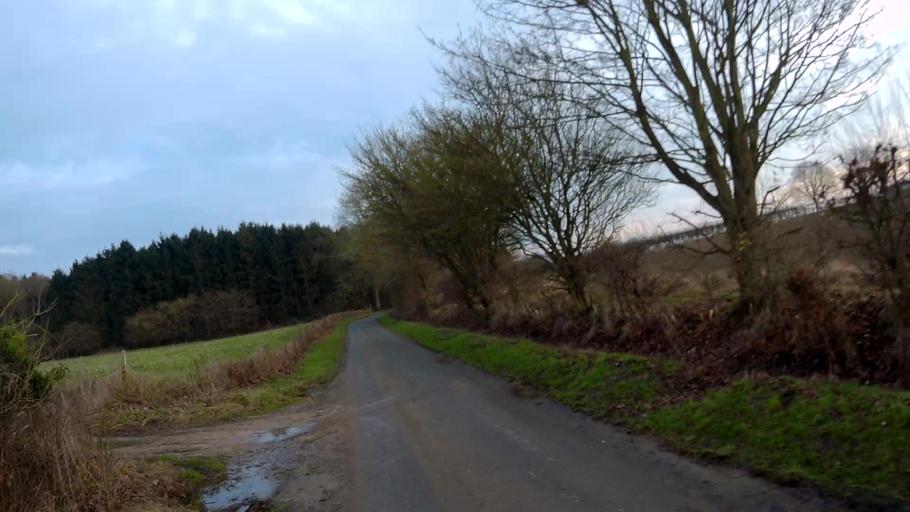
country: GB
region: England
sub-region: Lincolnshire
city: Bourne
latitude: 52.8193
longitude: -0.4005
